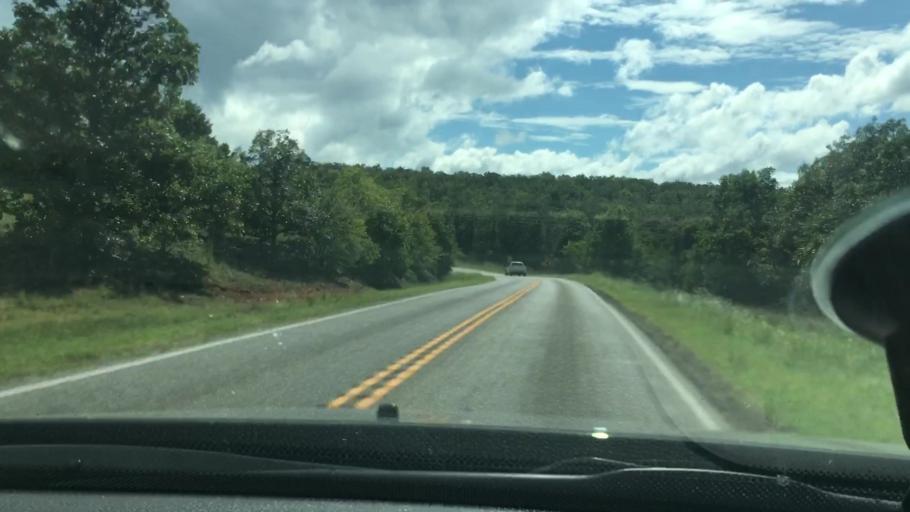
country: US
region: Oklahoma
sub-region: Sequoyah County
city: Vian
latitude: 35.6155
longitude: -94.9644
